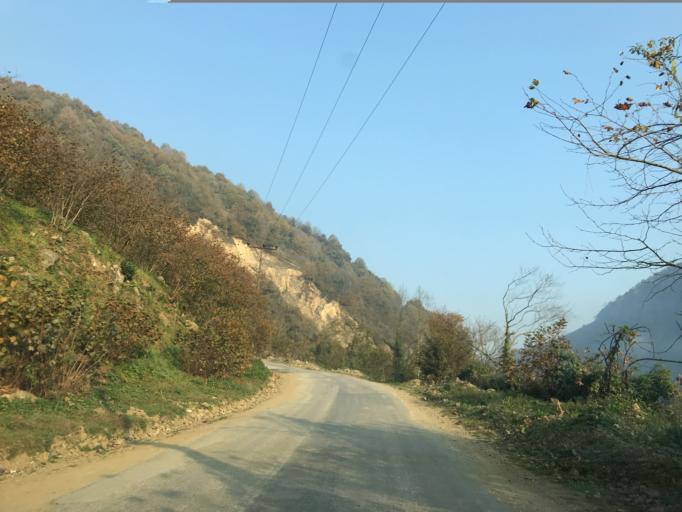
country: TR
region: Duzce
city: Cumayeri
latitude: 40.9204
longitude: 30.9292
